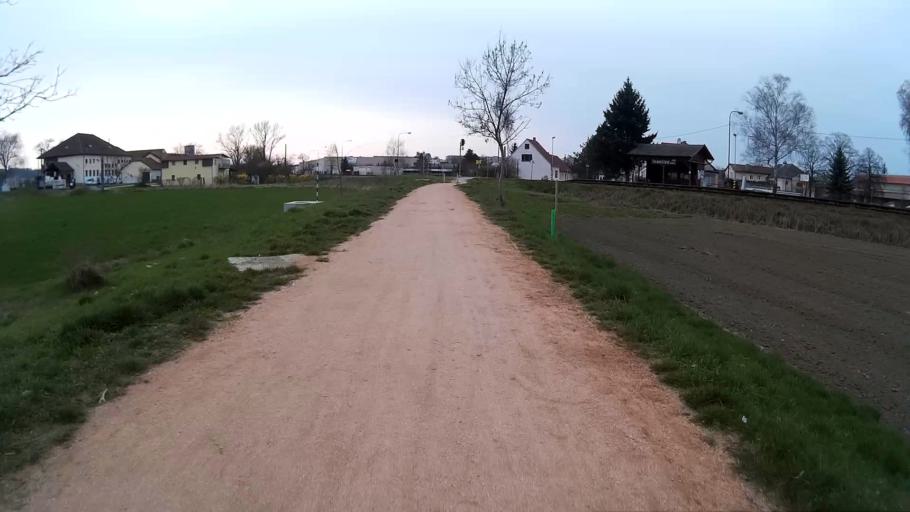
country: CZ
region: South Moravian
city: Ivancice
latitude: 49.0987
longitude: 16.3832
